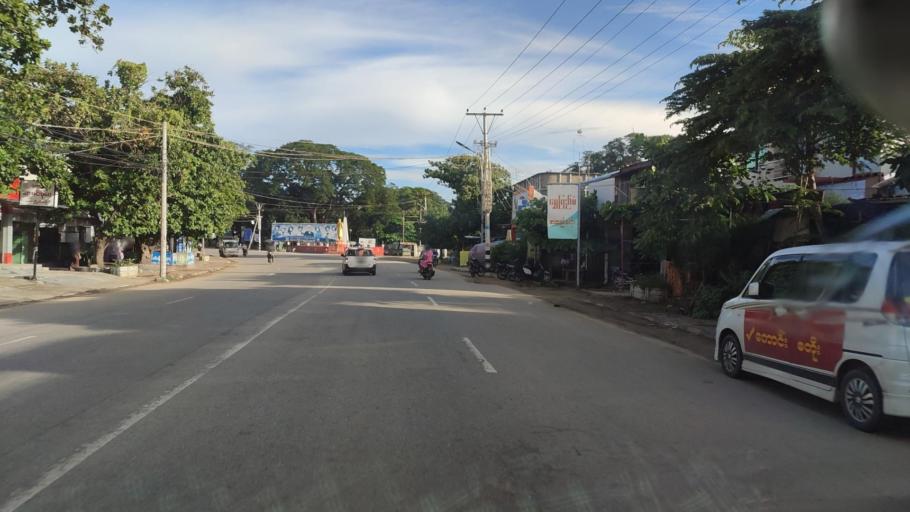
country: MM
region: Mandalay
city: Yamethin
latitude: 20.1299
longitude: 96.2016
